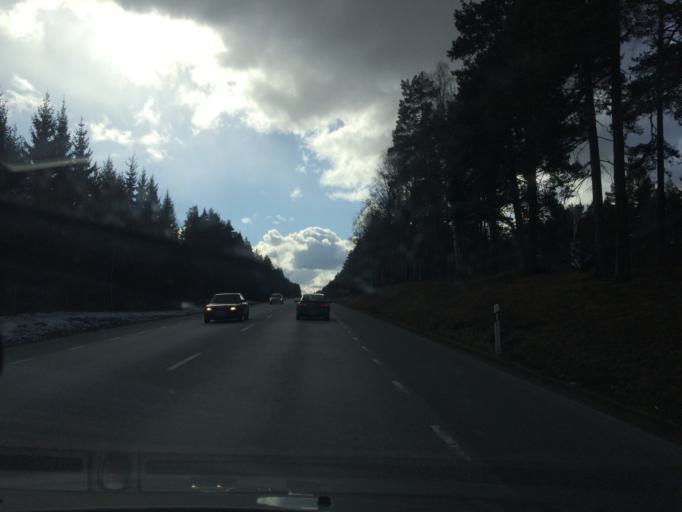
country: SE
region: Vaestra Goetaland
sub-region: Gotene Kommun
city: Goetene
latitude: 58.6168
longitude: 13.6586
